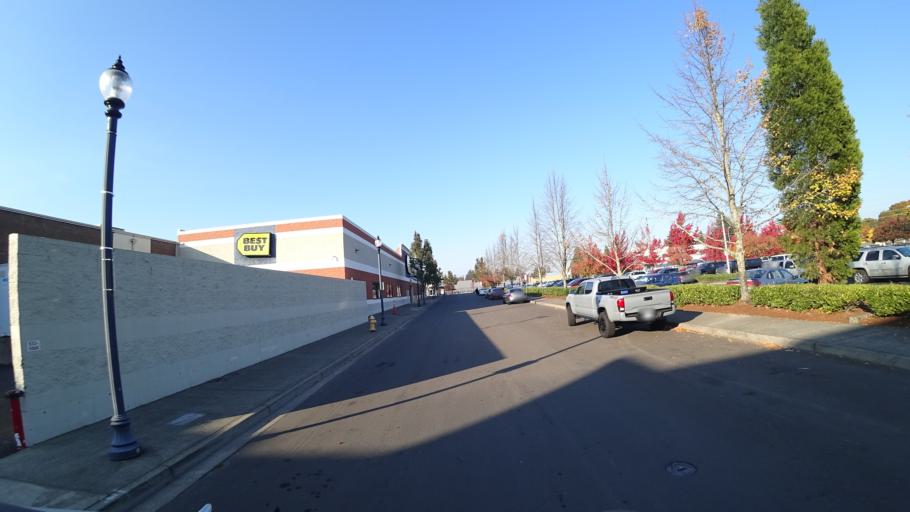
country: US
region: Oregon
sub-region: Multnomah County
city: Gresham
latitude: 45.5049
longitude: -122.4370
